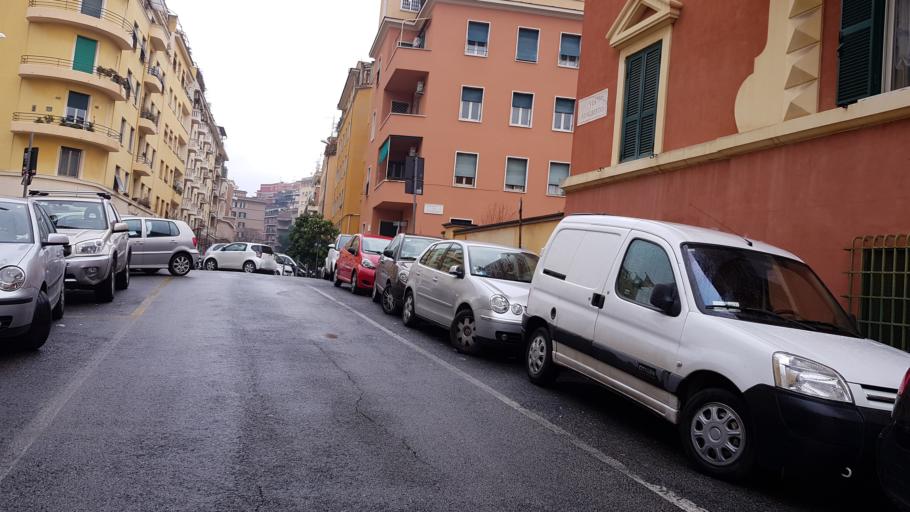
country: IT
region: Latium
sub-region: Citta metropolitana di Roma Capitale
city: Rome
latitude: 41.9099
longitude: 12.5230
